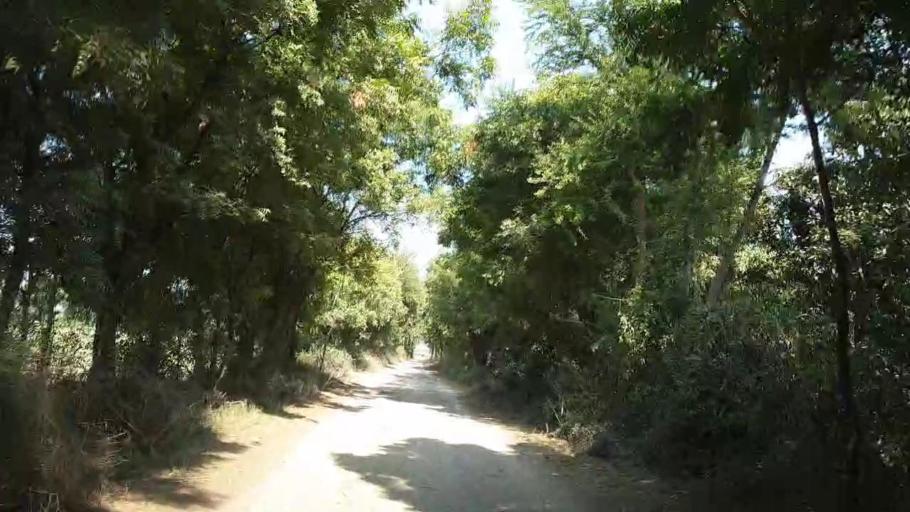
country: PK
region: Sindh
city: Bhit Shah
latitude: 25.7514
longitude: 68.4790
